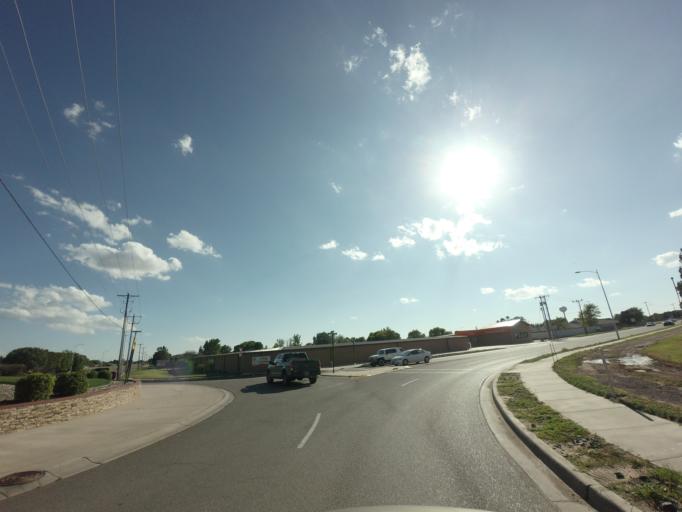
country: US
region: New Mexico
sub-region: Curry County
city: Clovis
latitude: 34.4340
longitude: -103.1787
